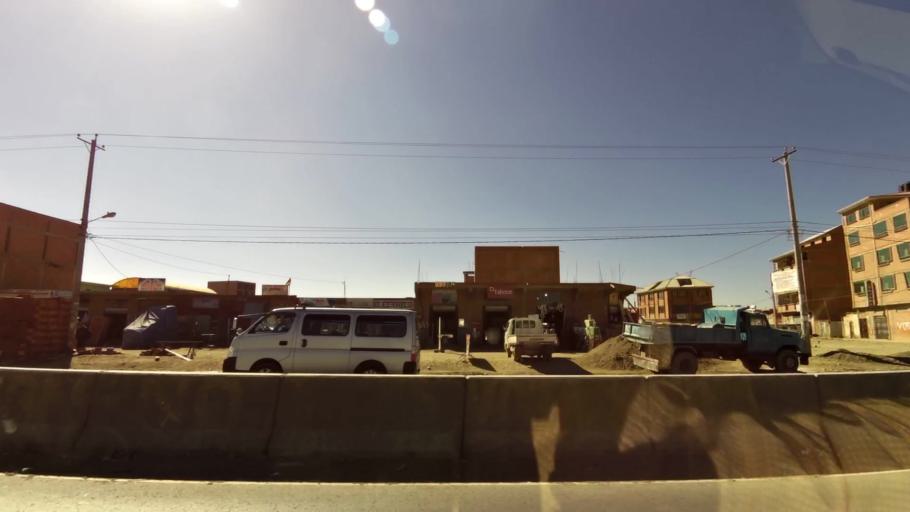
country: BO
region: La Paz
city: La Paz
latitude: -16.6169
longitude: -68.1827
